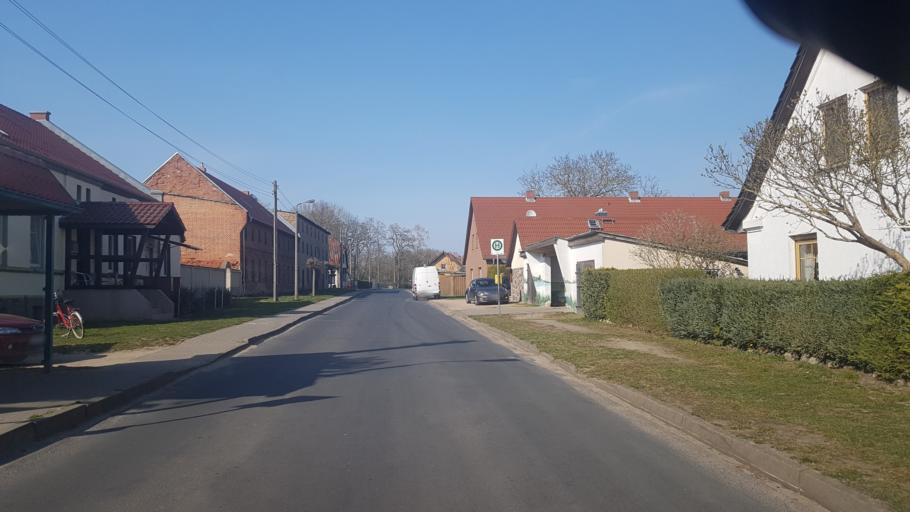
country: DE
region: Brandenburg
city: Prenzlau
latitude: 53.2188
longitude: 13.8413
